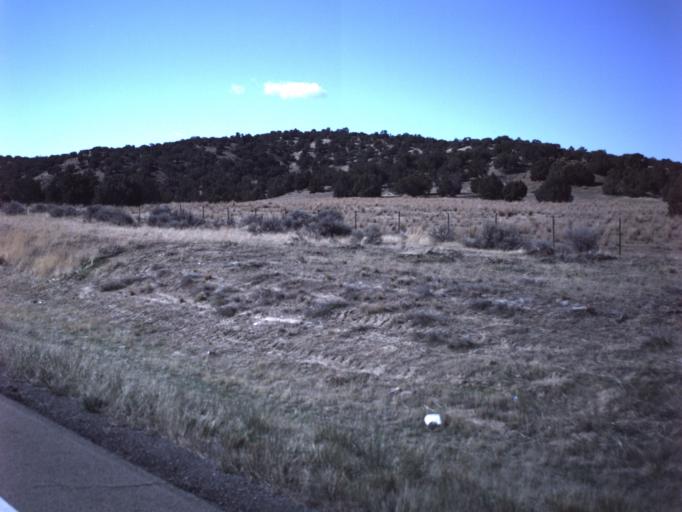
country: US
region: Utah
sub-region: Sanpete County
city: Gunnison
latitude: 39.3900
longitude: -111.9279
